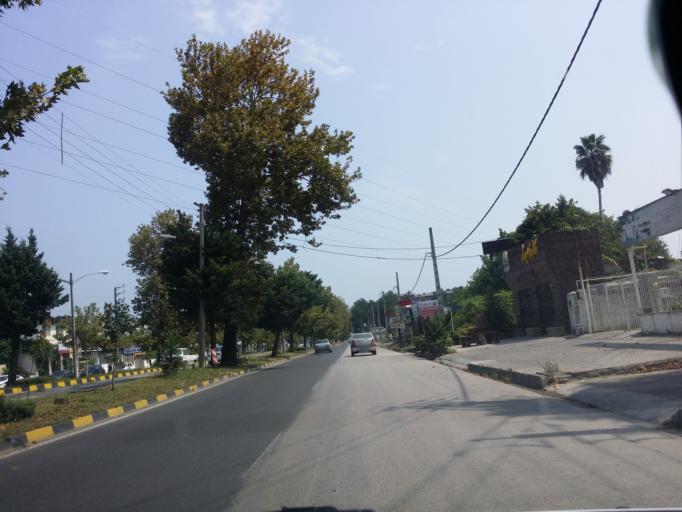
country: IR
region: Mazandaran
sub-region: Nowshahr
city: Nowshahr
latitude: 36.6551
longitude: 51.4643
